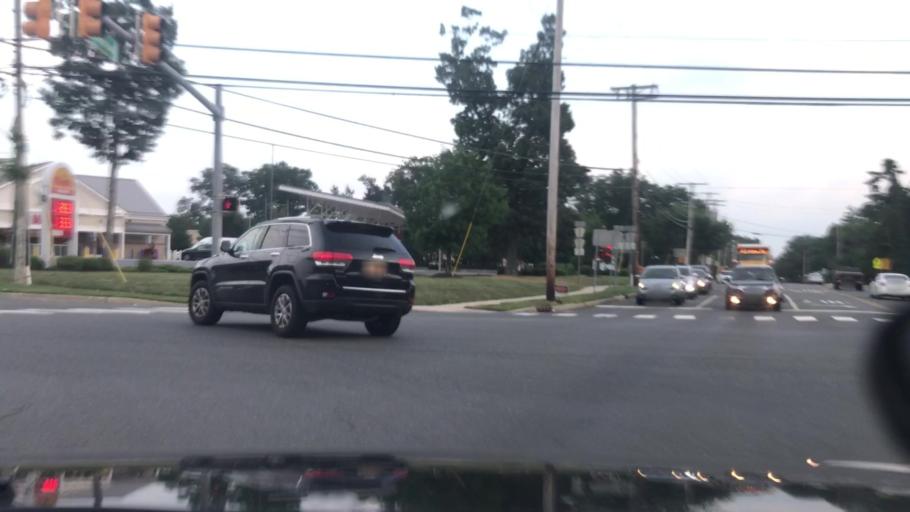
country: US
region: New Jersey
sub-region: Ocean County
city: Cedar Glen West
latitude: 40.0842
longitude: -74.2675
